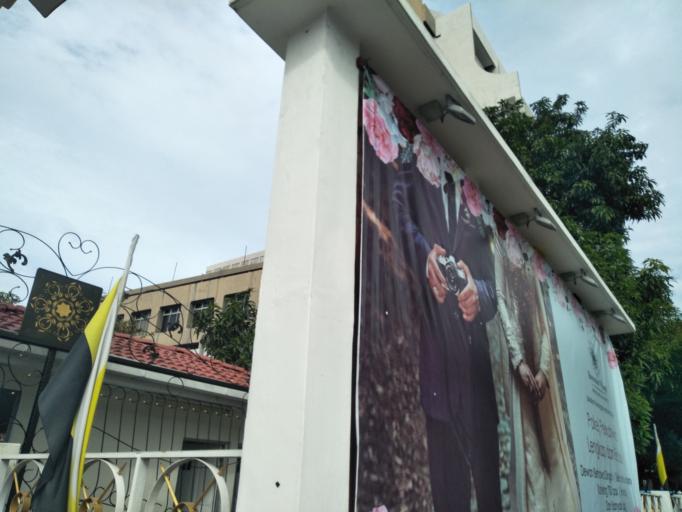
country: MY
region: Perak
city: Ipoh
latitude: 4.5977
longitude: 101.0806
